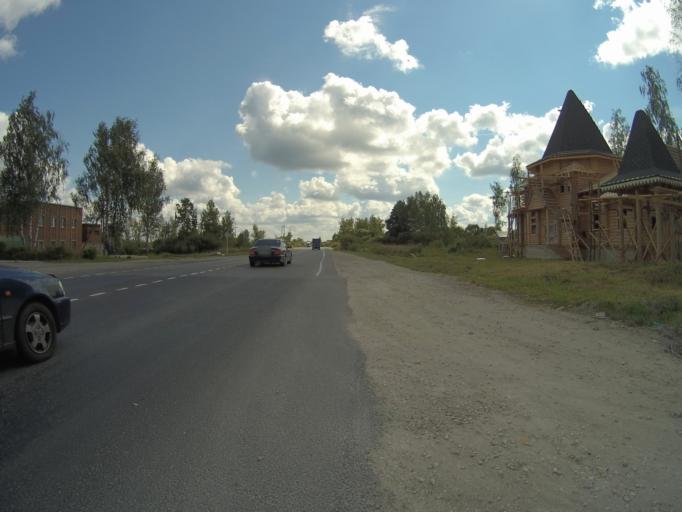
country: RU
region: Vladimir
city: Kommunar
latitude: 56.0480
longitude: 40.5345
